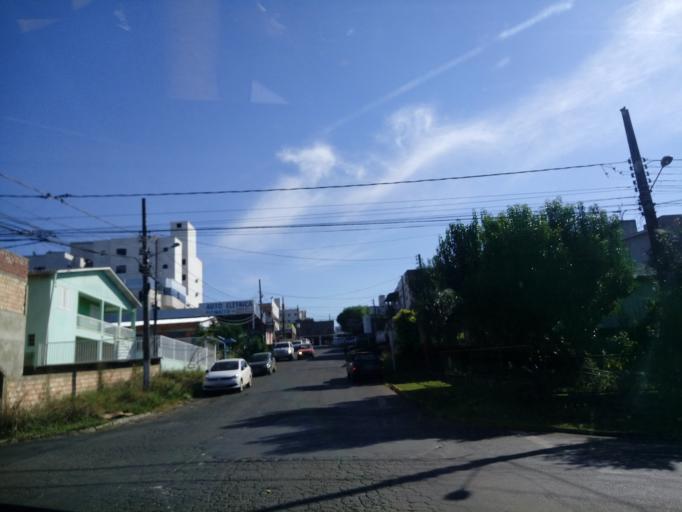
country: BR
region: Santa Catarina
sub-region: Chapeco
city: Chapeco
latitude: -27.0972
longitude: -52.6694
